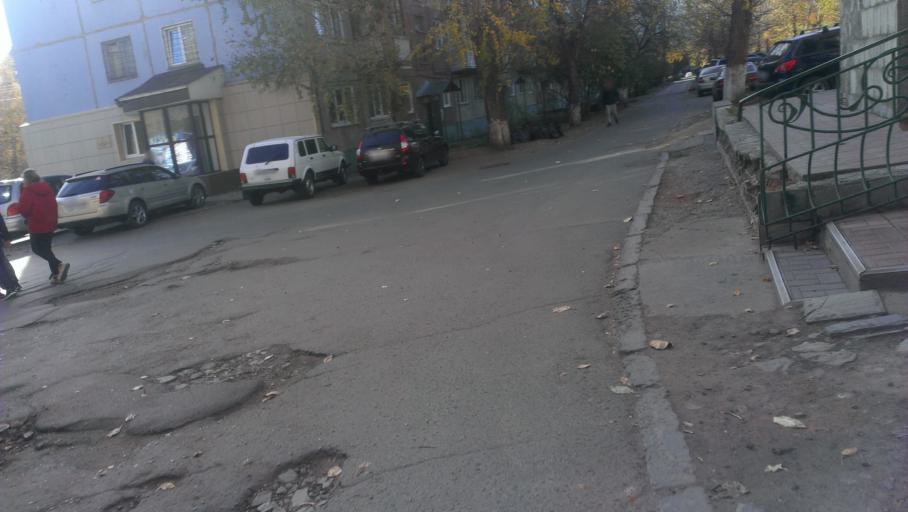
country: RU
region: Altai Krai
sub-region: Gorod Barnaulskiy
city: Barnaul
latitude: 53.3494
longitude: 83.6890
